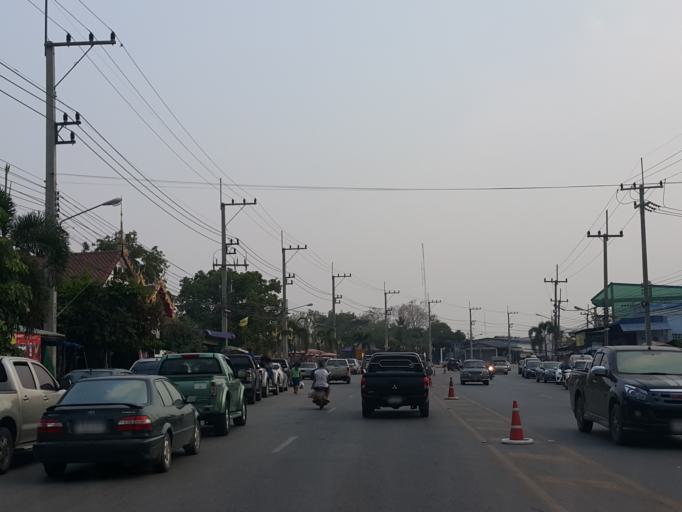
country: TH
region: Uthai Thani
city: Huai Khot
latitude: 15.1802
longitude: 99.6974
